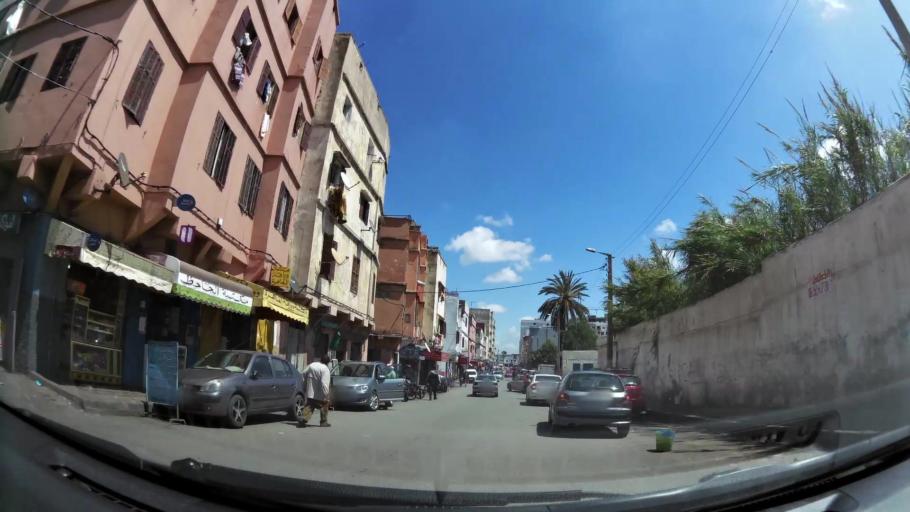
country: MA
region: Grand Casablanca
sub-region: Casablanca
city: Casablanca
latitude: 33.5677
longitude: -7.5993
